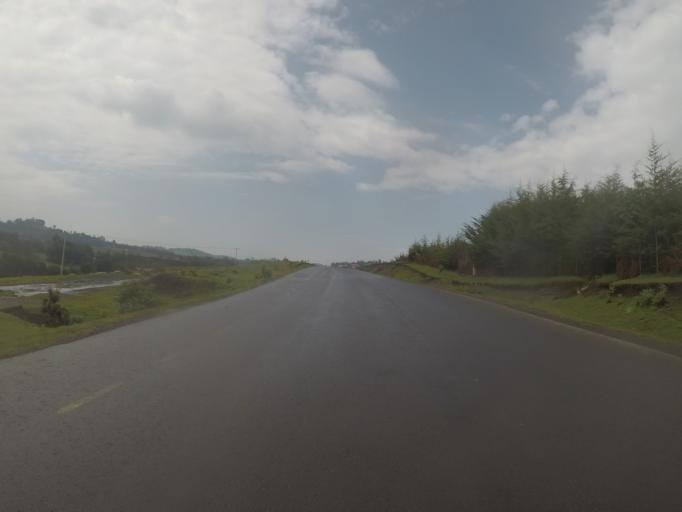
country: ET
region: Amhara
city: Debark'
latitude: 13.1314
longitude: 37.8916
